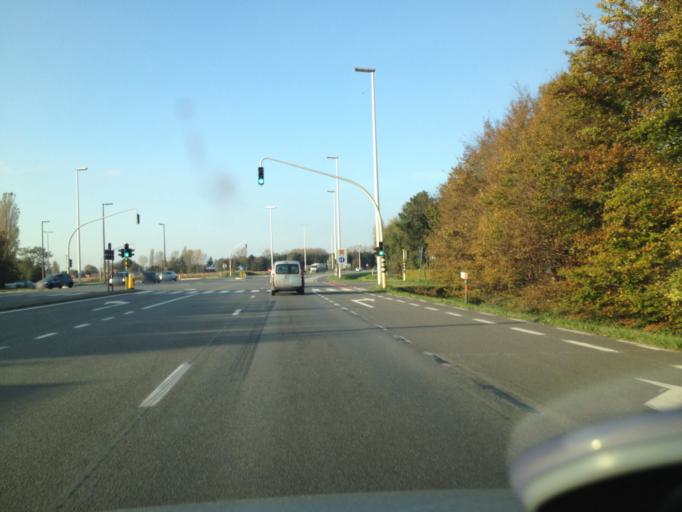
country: BE
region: Flanders
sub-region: Provincie Oost-Vlaanderen
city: Zelzate
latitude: 51.2033
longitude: 3.8248
